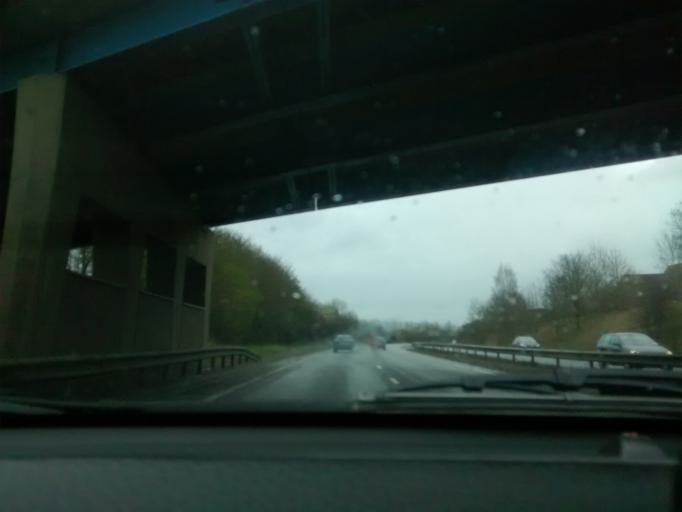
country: GB
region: England
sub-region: Suffolk
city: Stowmarket
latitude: 52.1952
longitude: 1.0106
